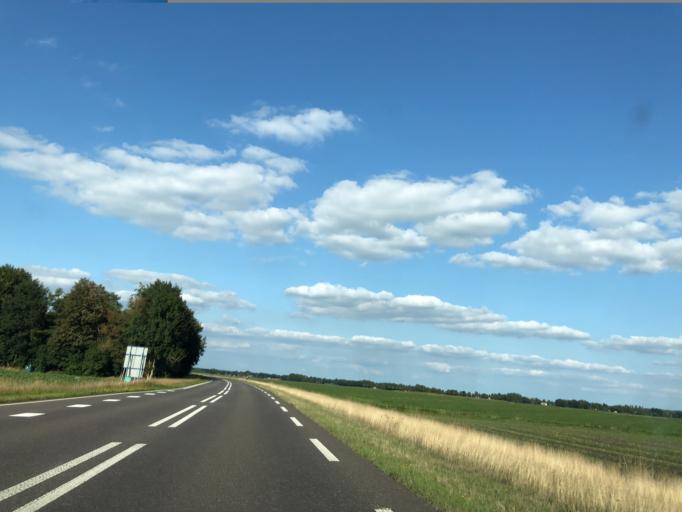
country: NL
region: Drenthe
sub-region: Gemeente Borger-Odoorn
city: Borger
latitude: 52.9347
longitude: 6.8543
